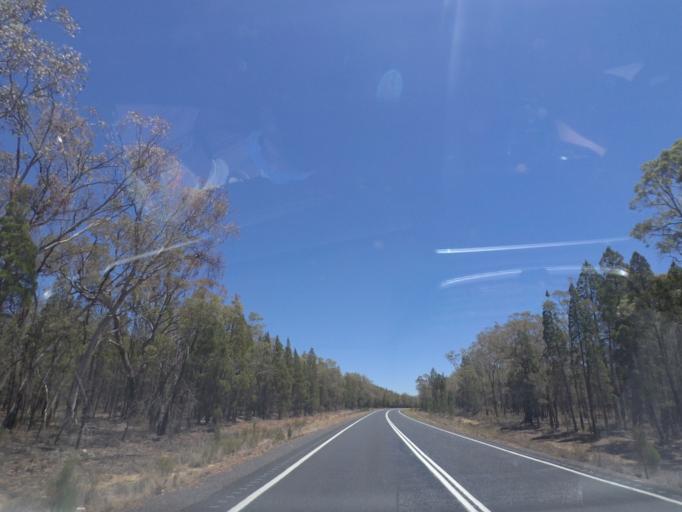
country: AU
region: New South Wales
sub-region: Warrumbungle Shire
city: Coonabarabran
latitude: -31.1968
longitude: 149.3498
